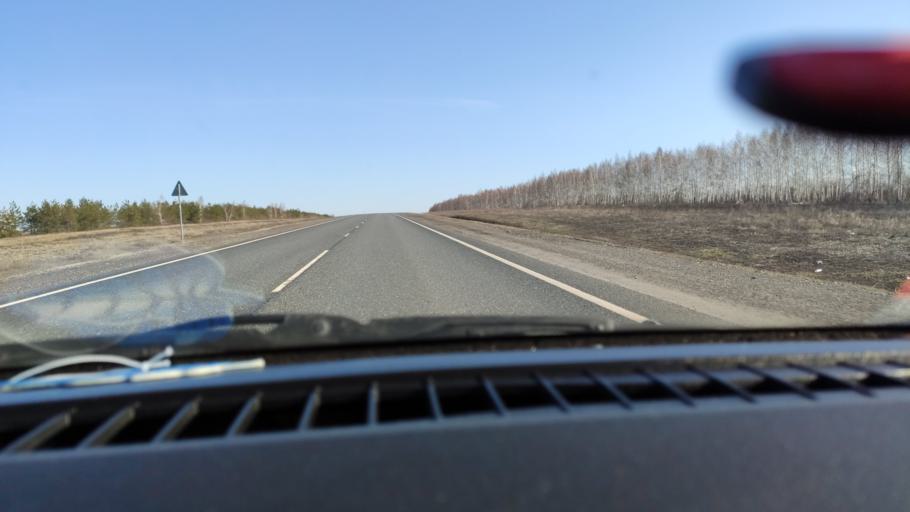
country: RU
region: Samara
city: Syzran'
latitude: 52.8898
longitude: 48.2946
